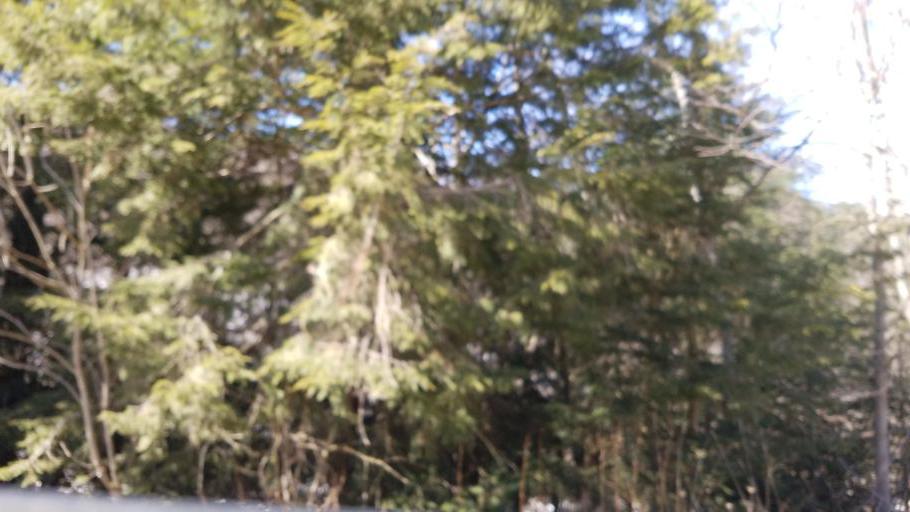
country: US
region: Pennsylvania
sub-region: Tioga County
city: Westfield
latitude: 41.9373
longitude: -77.7325
